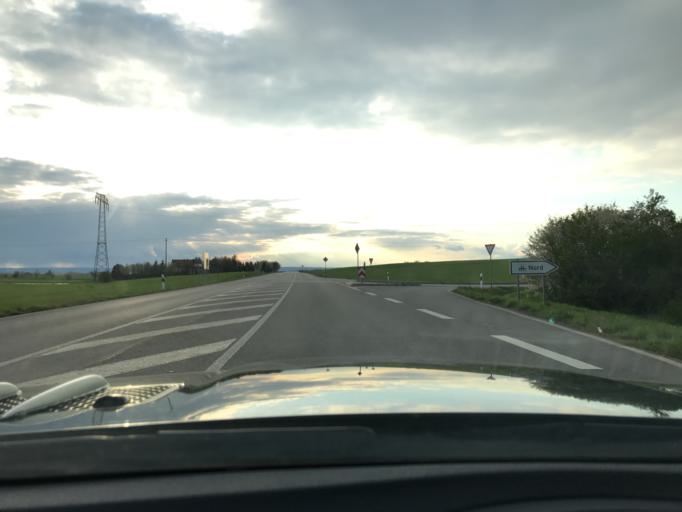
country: DE
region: Thuringia
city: Bad Langensalza
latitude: 51.1168
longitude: 10.6322
